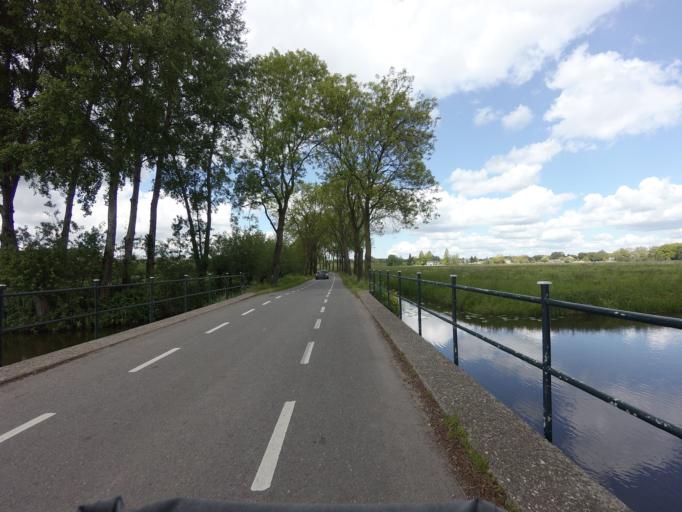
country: NL
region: South Holland
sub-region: Gemeente Leerdam
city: Leerdam
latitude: 51.8531
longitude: 5.0560
